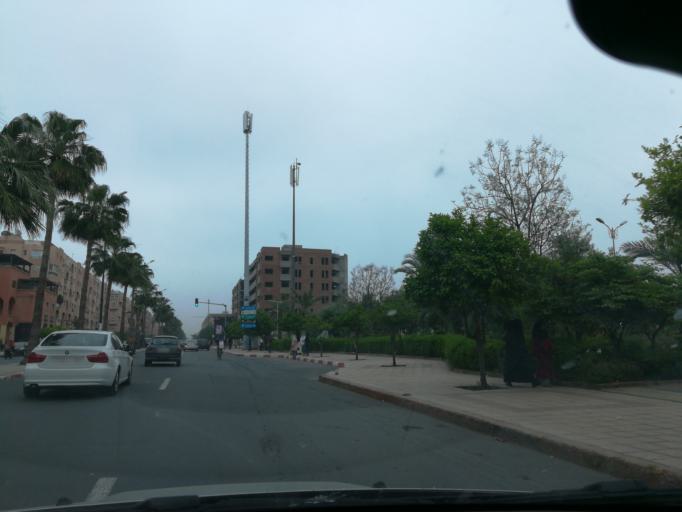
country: MA
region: Marrakech-Tensift-Al Haouz
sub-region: Marrakech
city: Marrakesh
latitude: 31.6619
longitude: -8.0077
